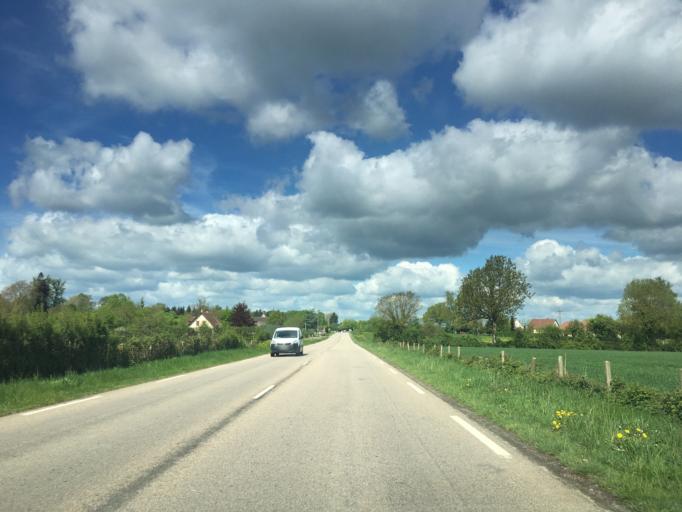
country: FR
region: Lower Normandy
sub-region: Departement de l'Orne
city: Aube-sur-Rile
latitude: 48.8384
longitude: 0.5235
